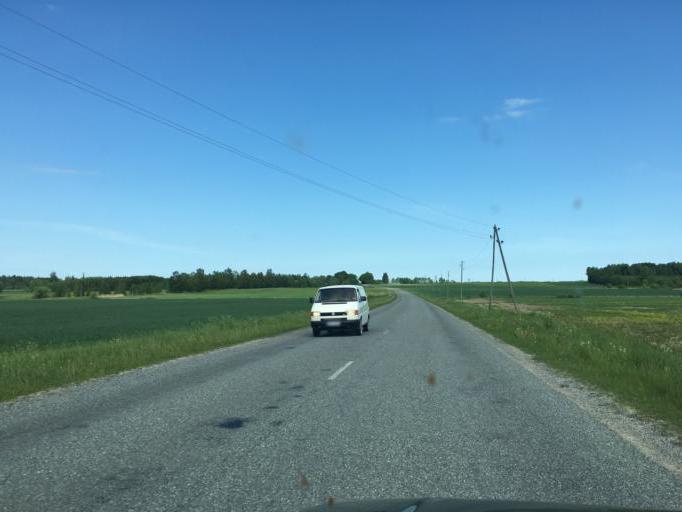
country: LV
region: Talsu Rajons
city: Valdemarpils
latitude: 57.3669
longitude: 22.4873
